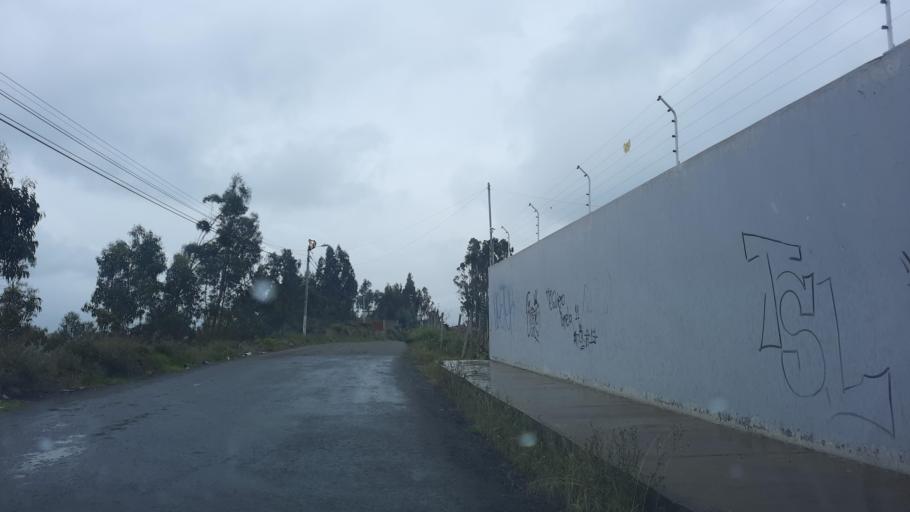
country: EC
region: Chimborazo
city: Riobamba
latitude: -1.6873
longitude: -78.6566
